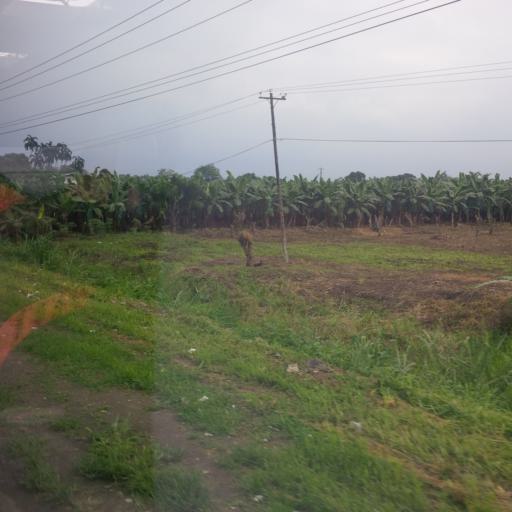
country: EC
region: Canar
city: La Troncal
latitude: -2.3394
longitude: -79.3862
